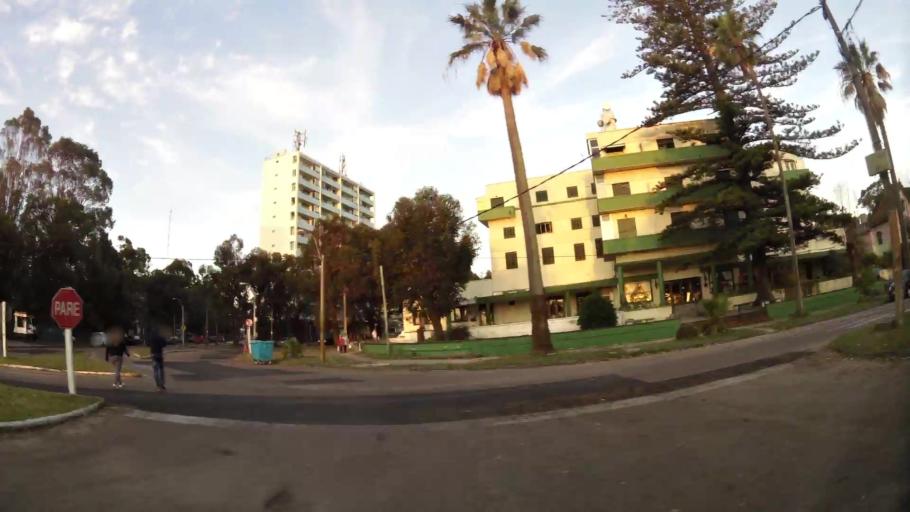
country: UY
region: Canelones
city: Atlantida
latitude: -34.7757
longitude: -55.7628
